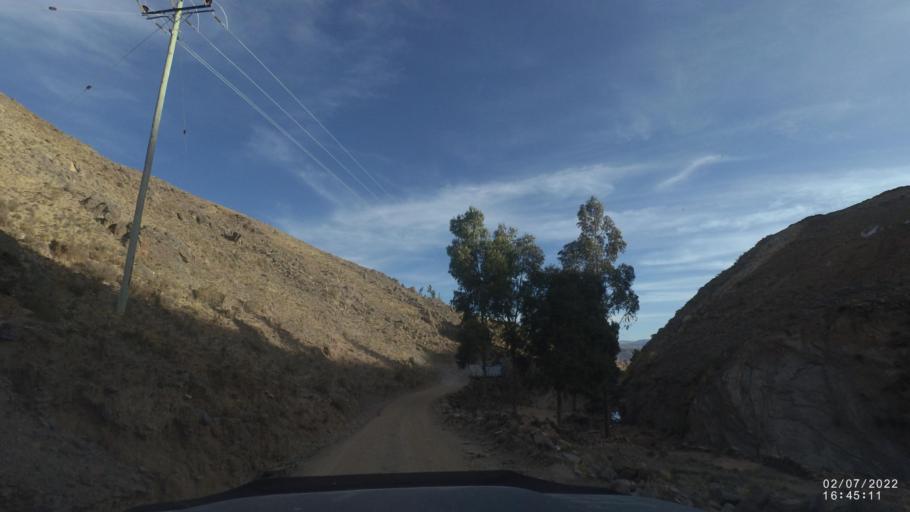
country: BO
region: Cochabamba
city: Irpa Irpa
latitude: -17.9752
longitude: -66.5100
